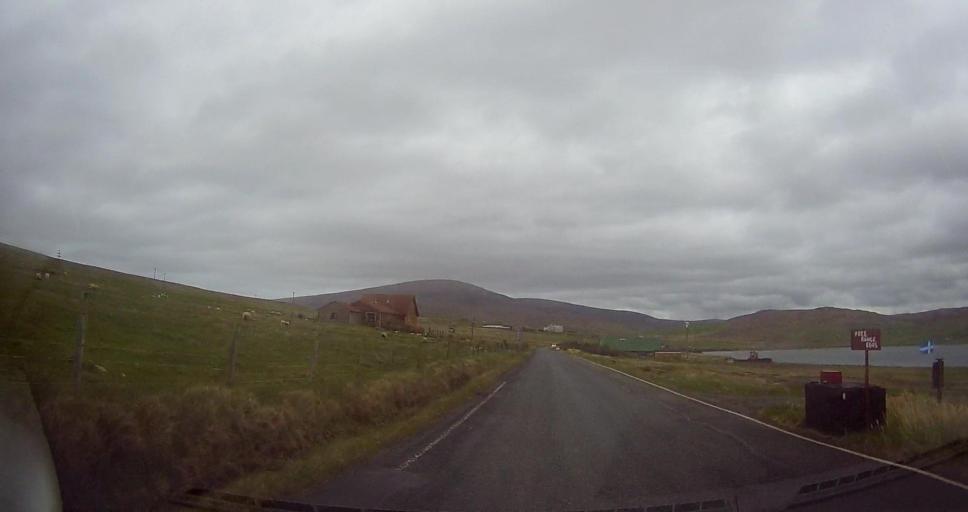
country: GB
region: Scotland
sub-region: Shetland Islands
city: Lerwick
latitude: 60.4861
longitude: -1.4684
